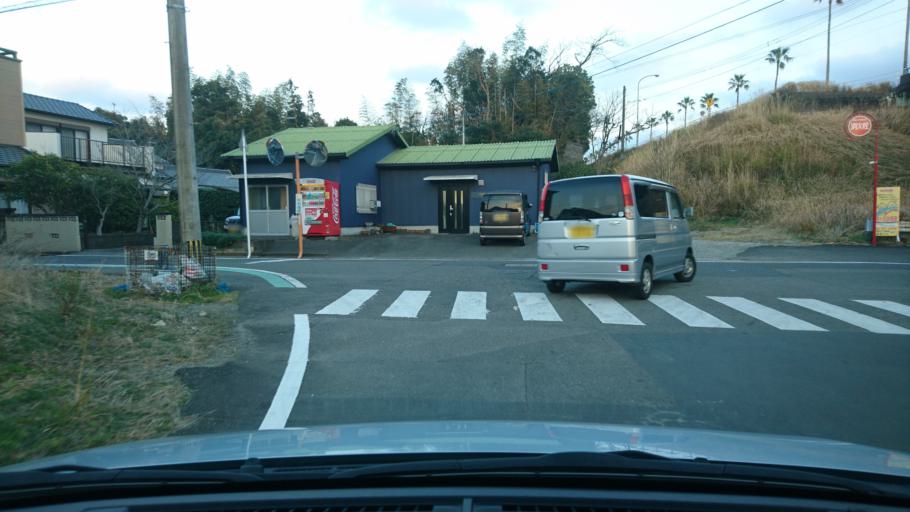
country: JP
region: Miyazaki
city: Miyazaki-shi
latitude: 31.8681
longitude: 131.4276
